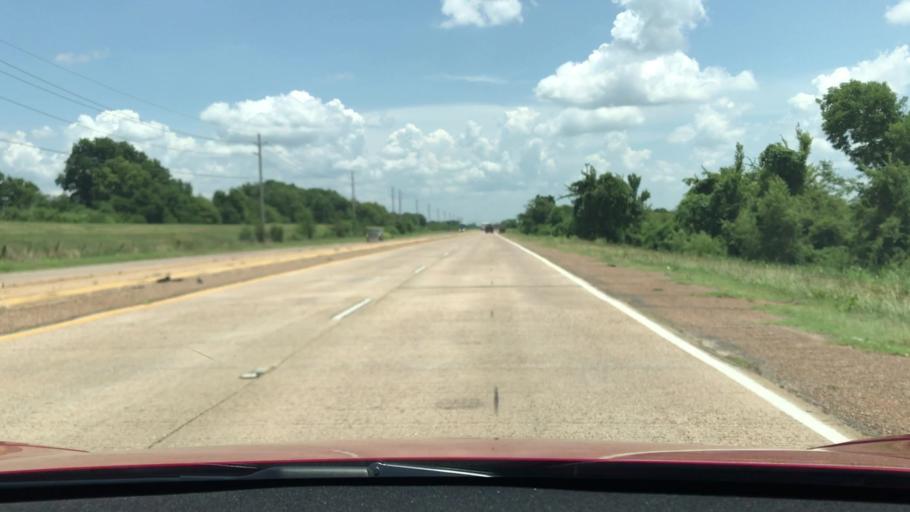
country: US
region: Louisiana
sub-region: Bossier Parish
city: Bossier City
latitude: 32.3871
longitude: -93.6777
